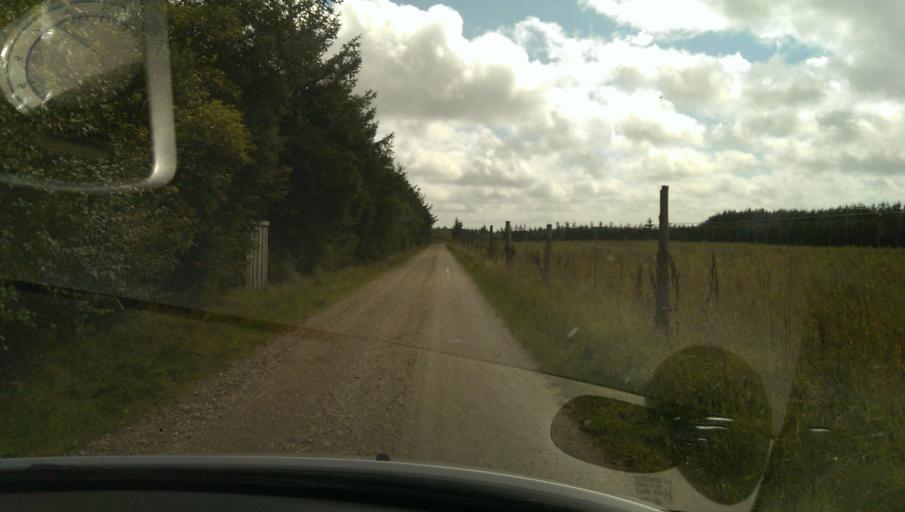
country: DK
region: South Denmark
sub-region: Varde Kommune
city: Varde
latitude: 55.6054
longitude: 8.4510
